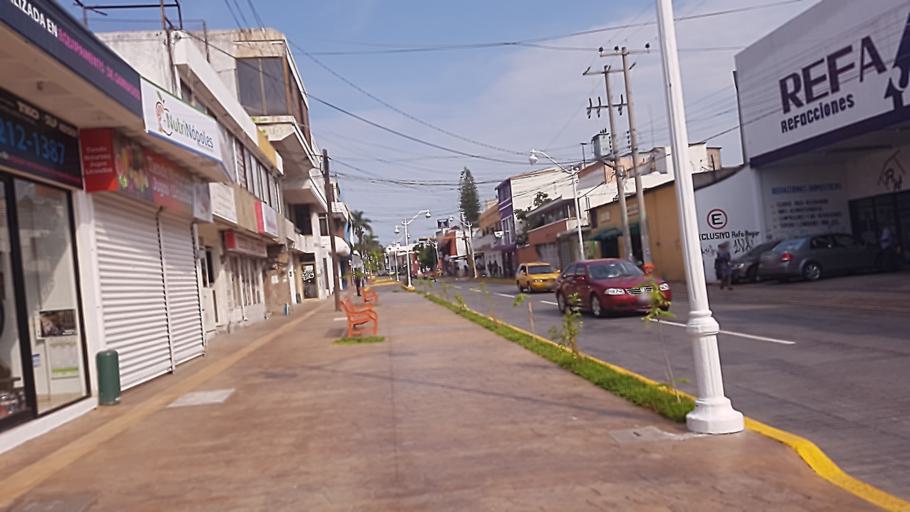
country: MX
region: Nayarit
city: Tepic
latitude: 21.5096
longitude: -104.8956
